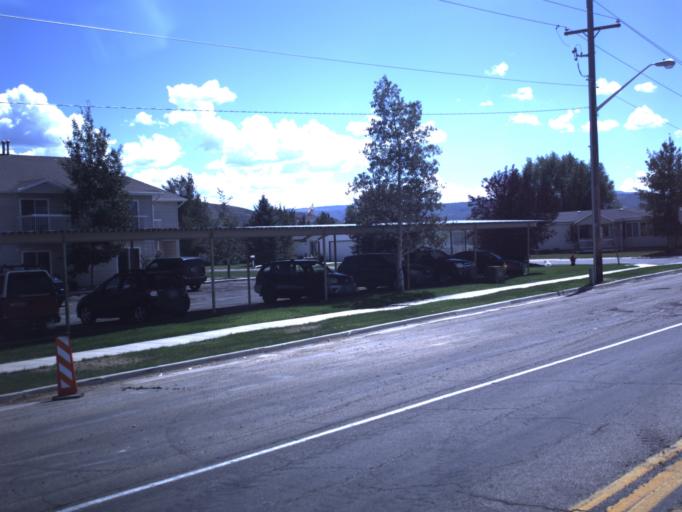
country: US
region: Utah
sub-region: Summit County
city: Kamas
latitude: 40.6336
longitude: -111.2808
